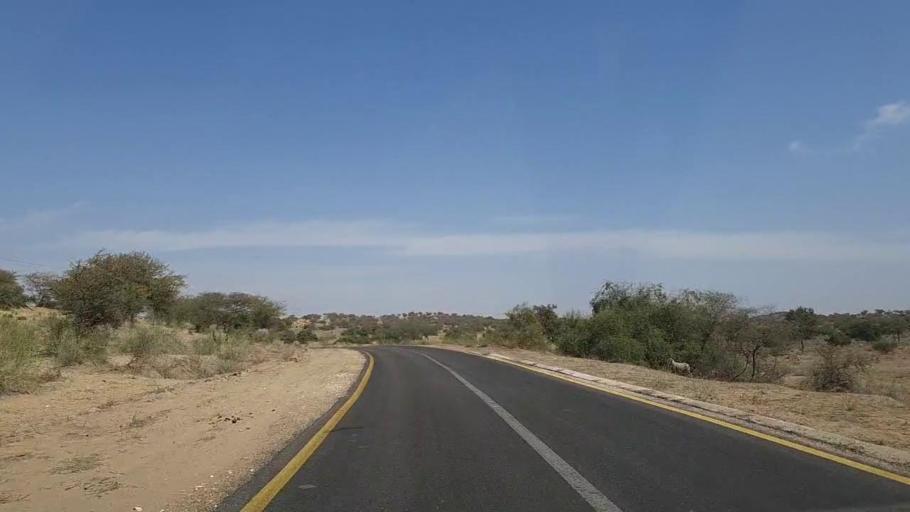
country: PK
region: Sindh
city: Mithi
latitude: 24.9028
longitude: 69.8868
